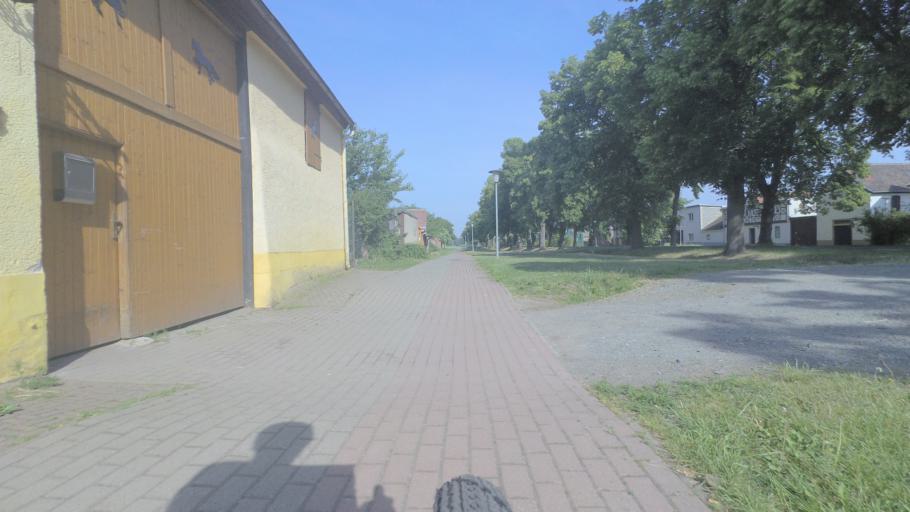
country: DE
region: Saxony-Anhalt
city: Nachterstedt
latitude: 51.7654
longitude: 11.3482
